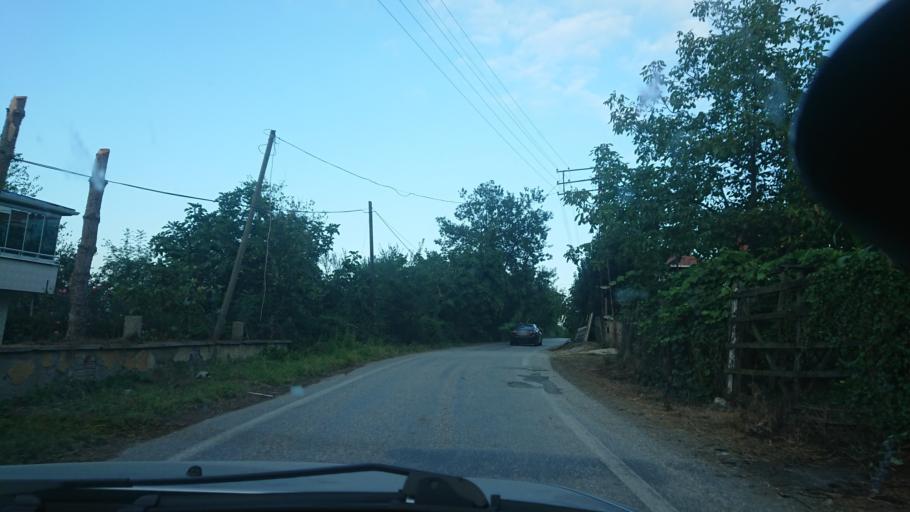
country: TR
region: Samsun
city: Tekkekoy
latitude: 41.1717
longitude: 36.5321
